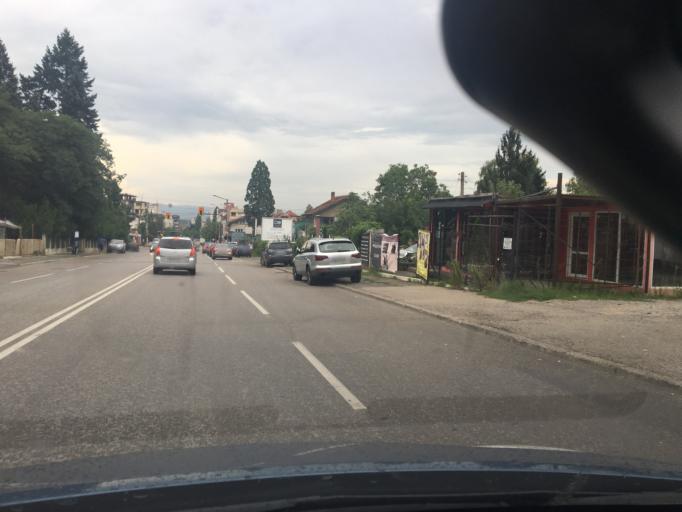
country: BG
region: Sofia-Capital
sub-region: Stolichna Obshtina
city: Sofia
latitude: 42.6590
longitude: 23.2648
